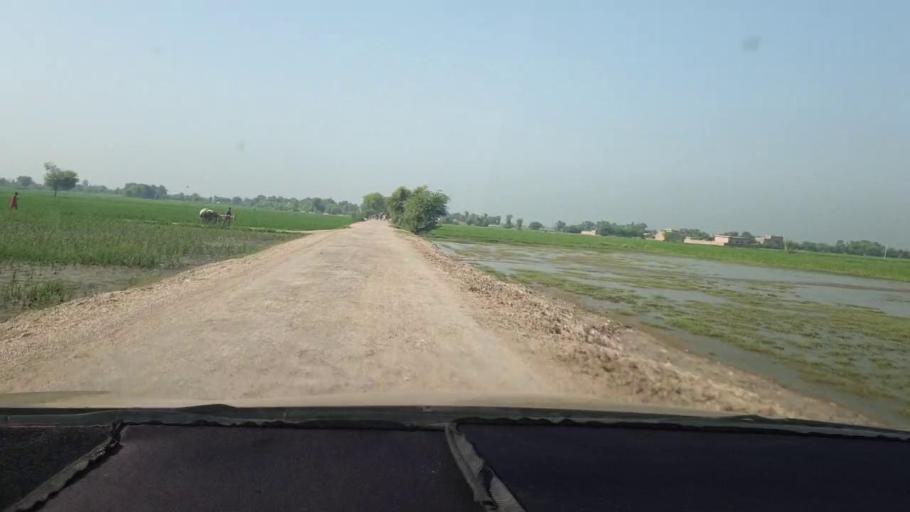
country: PK
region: Sindh
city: Kambar
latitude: 27.5749
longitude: 68.0876
